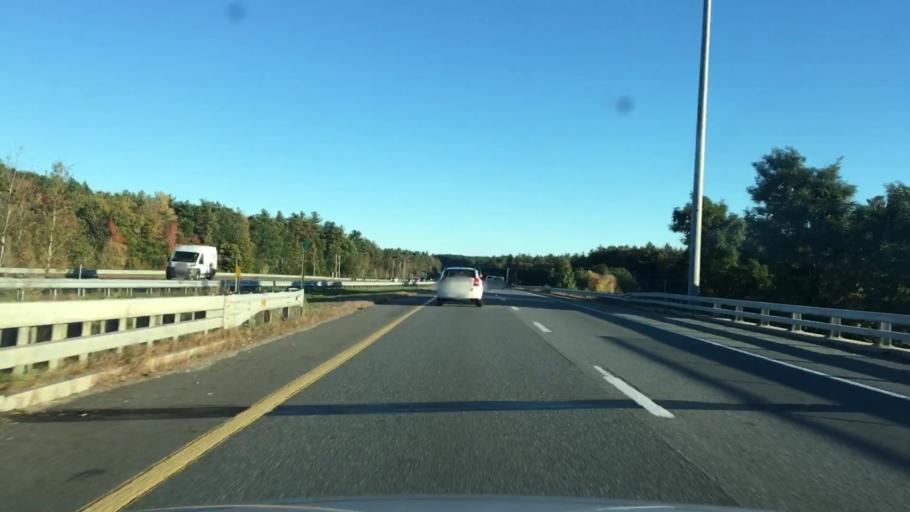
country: US
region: New Hampshire
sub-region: Rockingham County
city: Exeter
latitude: 42.9921
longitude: -70.9265
